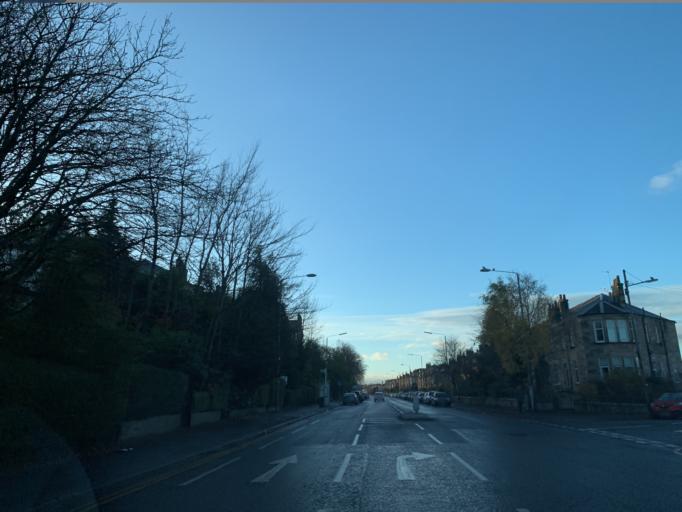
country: GB
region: Scotland
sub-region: East Renfrewshire
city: Giffnock
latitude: 55.8234
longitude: -4.2865
